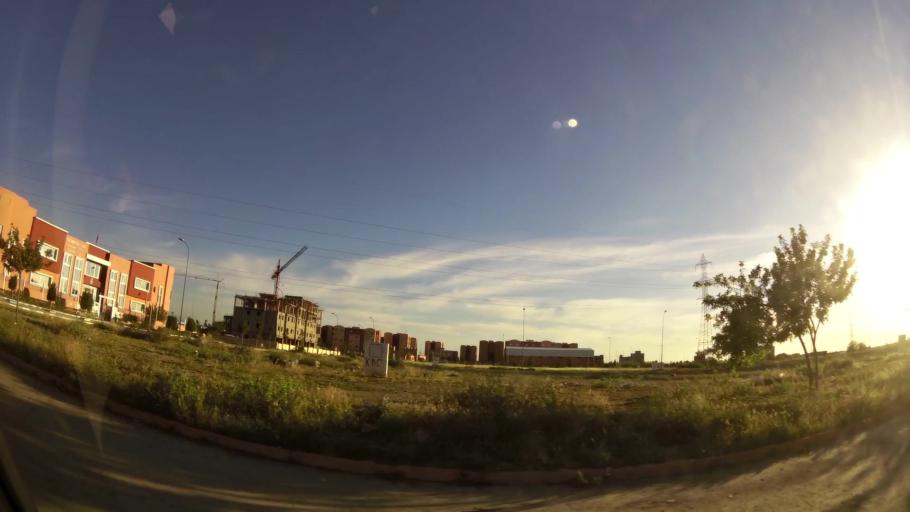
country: MA
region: Marrakech-Tensift-Al Haouz
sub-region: Marrakech
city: Marrakesh
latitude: 31.7439
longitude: -8.1248
